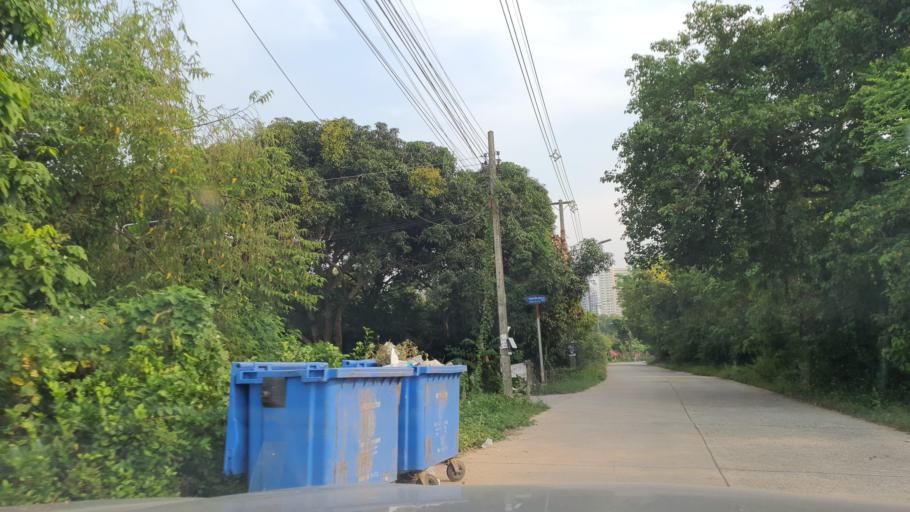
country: TH
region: Rayong
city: Rayong
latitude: 12.6113
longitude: 101.4009
